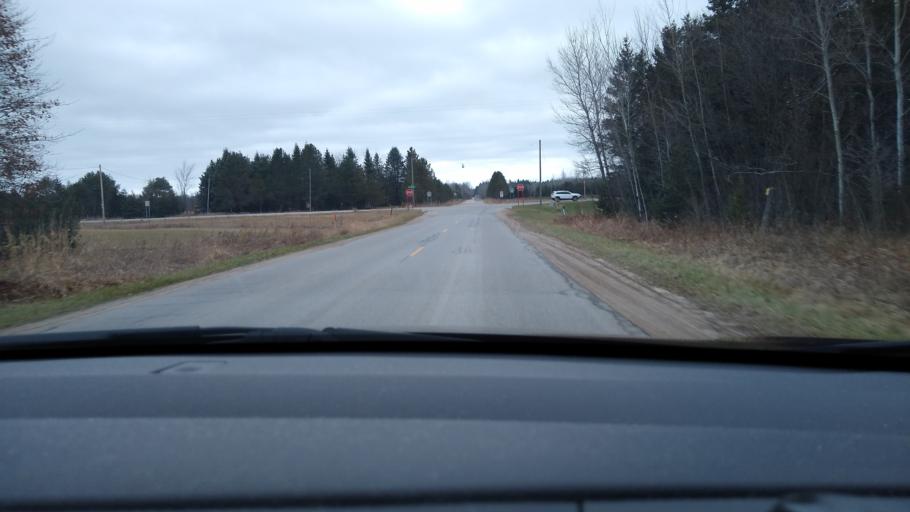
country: US
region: Michigan
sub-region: Missaukee County
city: Lake City
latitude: 44.3363
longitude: -85.0551
